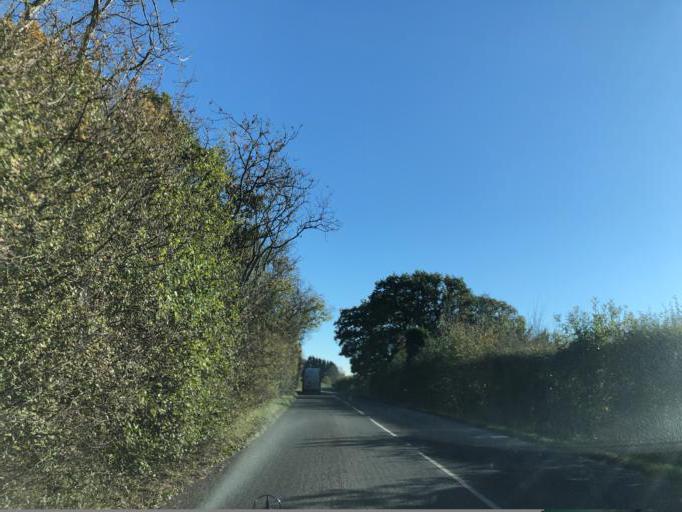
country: GB
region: England
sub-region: Warwickshire
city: Royal Leamington Spa
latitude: 52.2508
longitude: -1.5178
